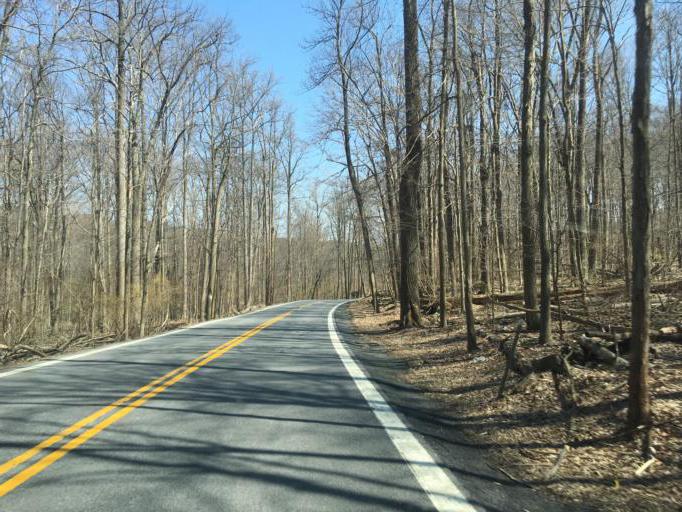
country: US
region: Maryland
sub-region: Frederick County
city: Thurmont
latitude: 39.6357
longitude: -77.4838
